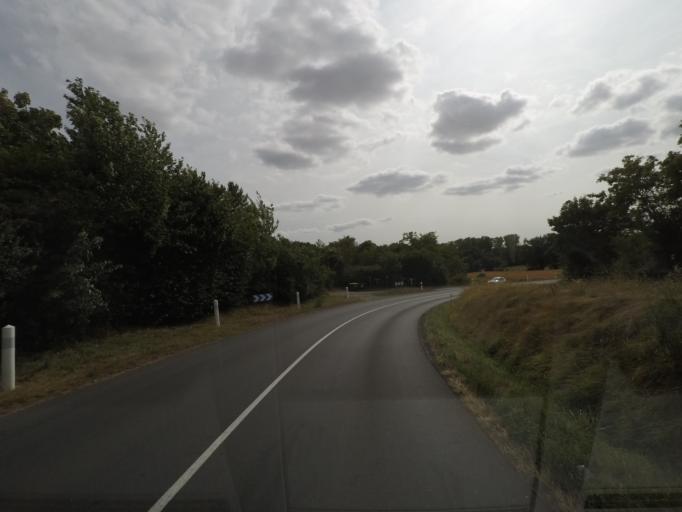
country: FR
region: Poitou-Charentes
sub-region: Departement de la Charente
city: Ruffec
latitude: 46.0244
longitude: 0.2331
